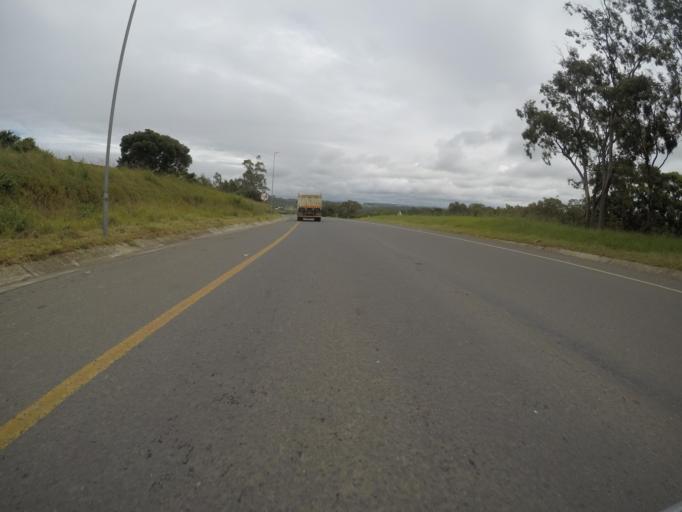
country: ZA
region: Eastern Cape
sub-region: Buffalo City Metropolitan Municipality
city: East London
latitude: -32.9395
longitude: 27.9507
